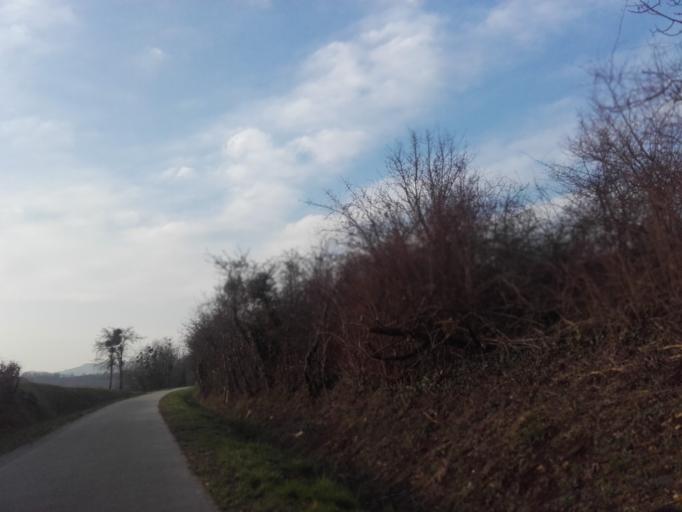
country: FR
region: Bourgogne
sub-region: Departement de la Cote-d'Or
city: Nolay
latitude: 46.9025
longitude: 4.6663
